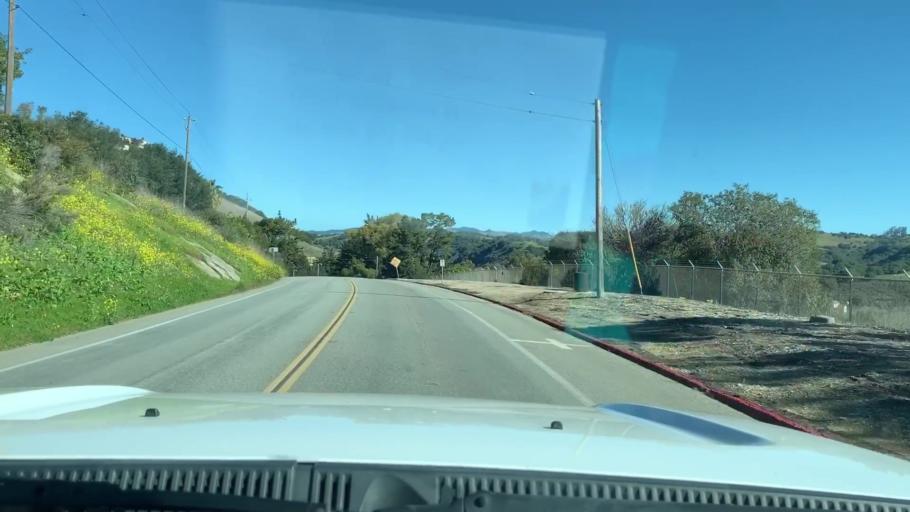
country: US
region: California
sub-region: San Luis Obispo County
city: Pismo Beach
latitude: 35.1441
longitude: -120.6359
